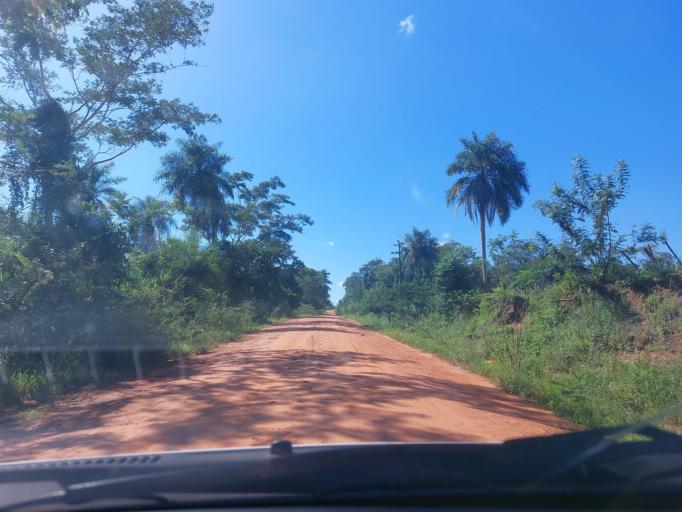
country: PY
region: San Pedro
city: Itacurubi del Rosario
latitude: -24.5454
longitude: -56.5850
